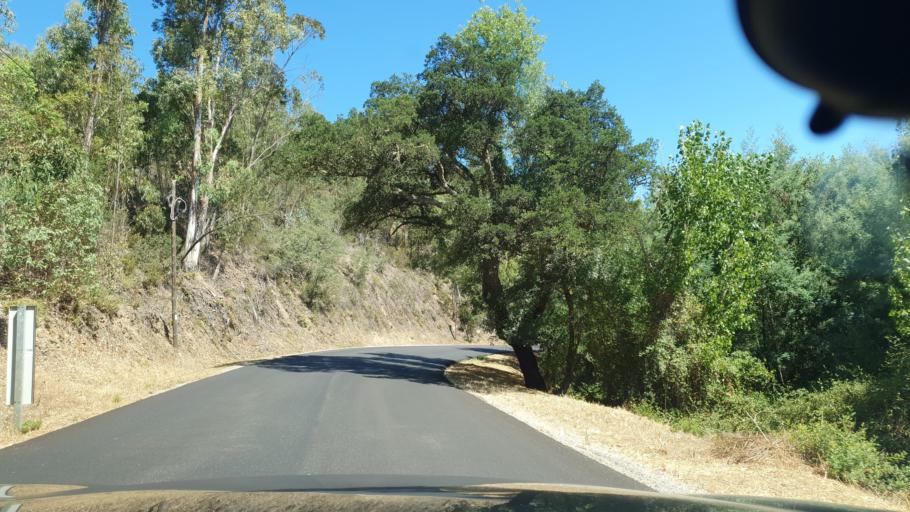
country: PT
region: Faro
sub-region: Monchique
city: Monchique
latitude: 37.4755
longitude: -8.4898
